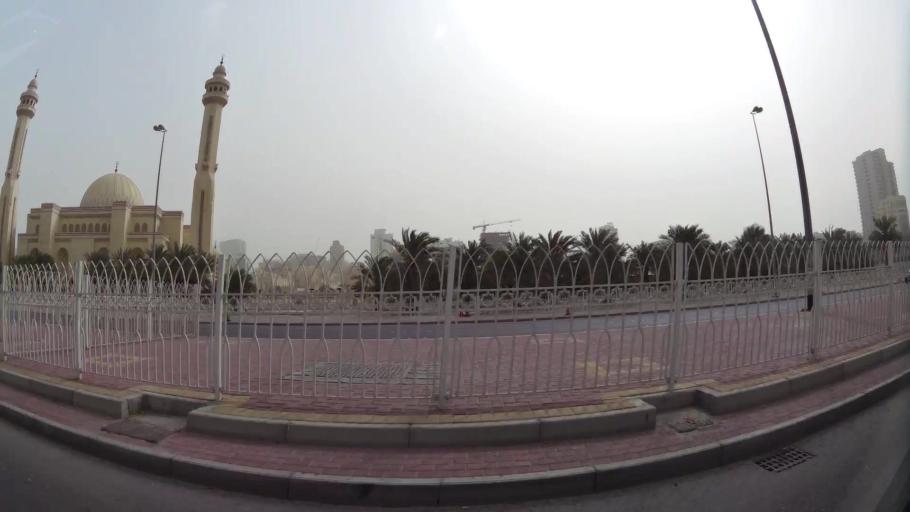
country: BH
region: Manama
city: Manama
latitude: 26.2178
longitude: 50.5971
